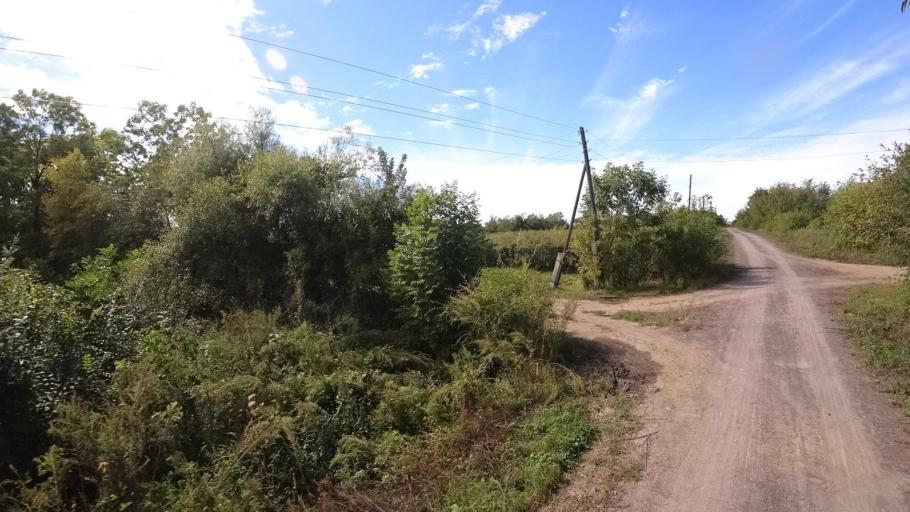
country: RU
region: Primorskiy
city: Yakovlevka
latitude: 44.4332
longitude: 133.5683
